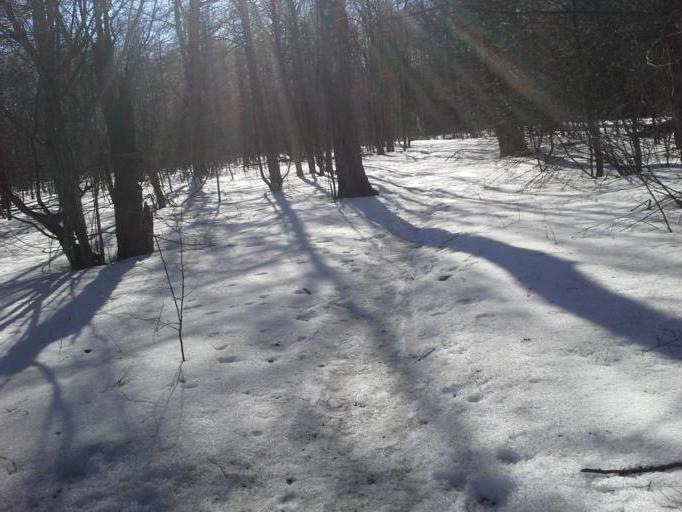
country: RU
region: Moscow
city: Yasenevo
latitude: 55.5975
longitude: 37.5001
